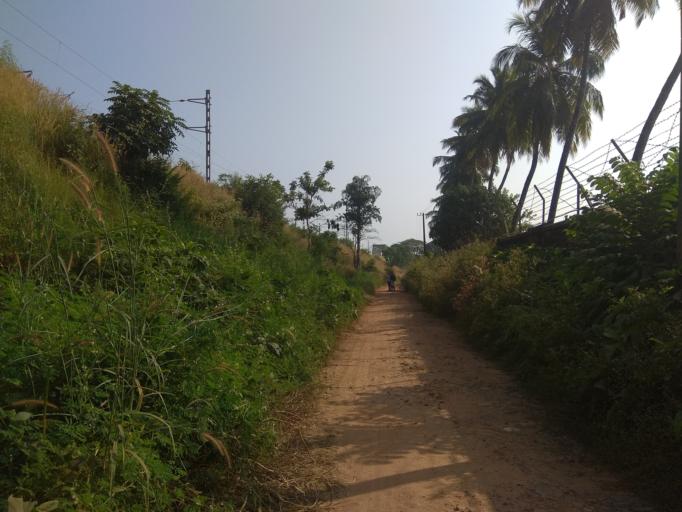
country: IN
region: Karnataka
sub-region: Dakshina Kannada
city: Ullal
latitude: 12.8453
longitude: 74.8559
